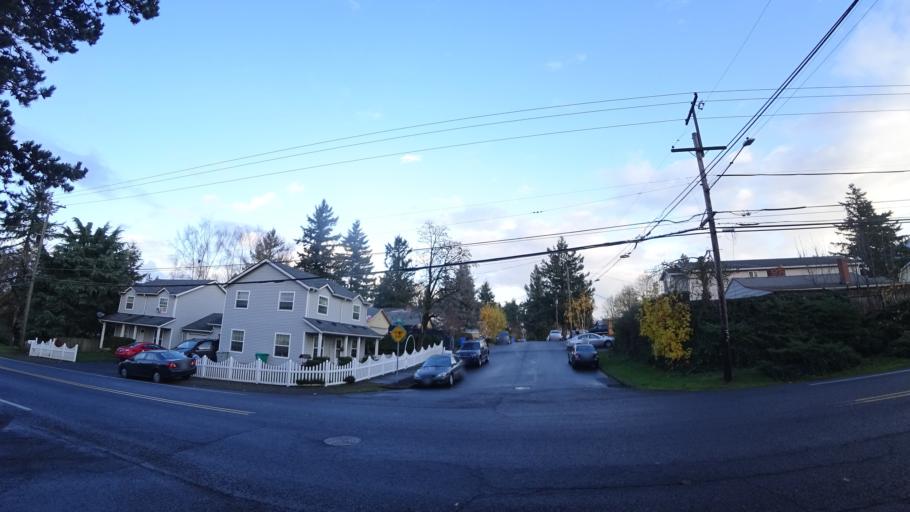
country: US
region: Oregon
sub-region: Multnomah County
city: Lents
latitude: 45.5161
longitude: -122.5430
